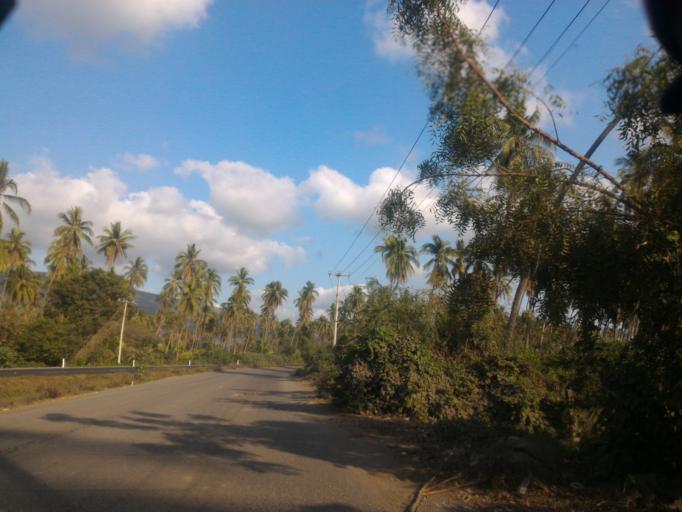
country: MX
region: Colima
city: Tecoman
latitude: 18.9325
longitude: -103.8611
